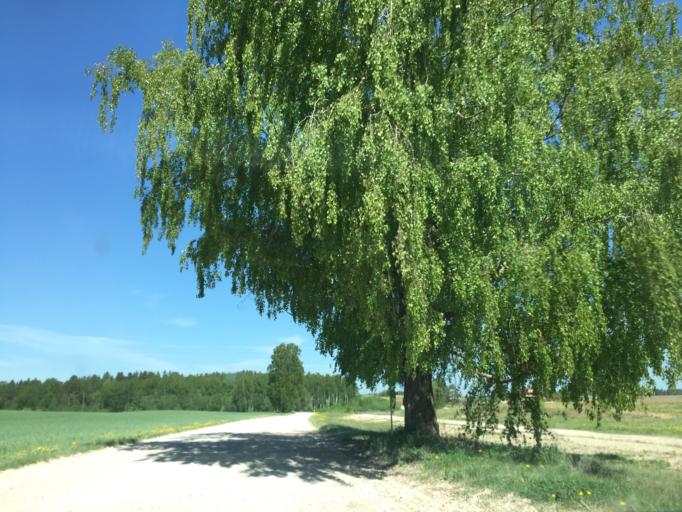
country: LV
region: Ikskile
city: Ikskile
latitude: 56.8601
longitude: 24.5004
